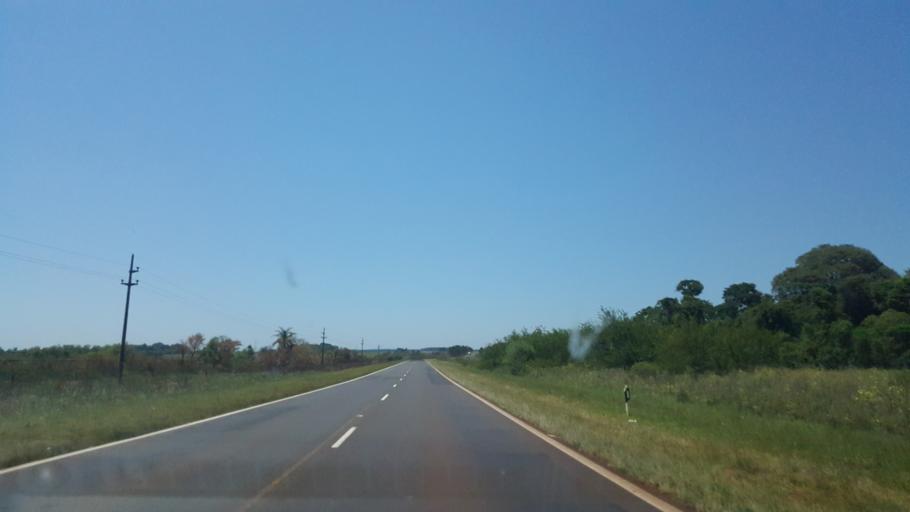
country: AR
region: Corrientes
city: Santo Tome
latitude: -28.3771
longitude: -56.1088
